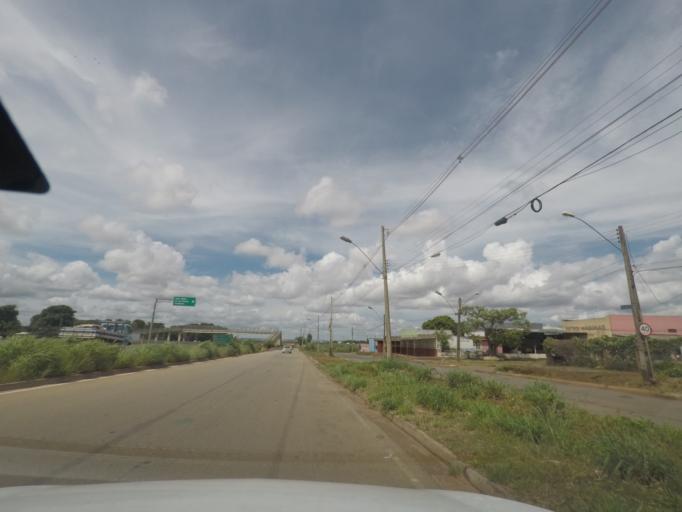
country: BR
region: Goias
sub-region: Goiania
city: Goiania
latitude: -16.7149
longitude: -49.3610
